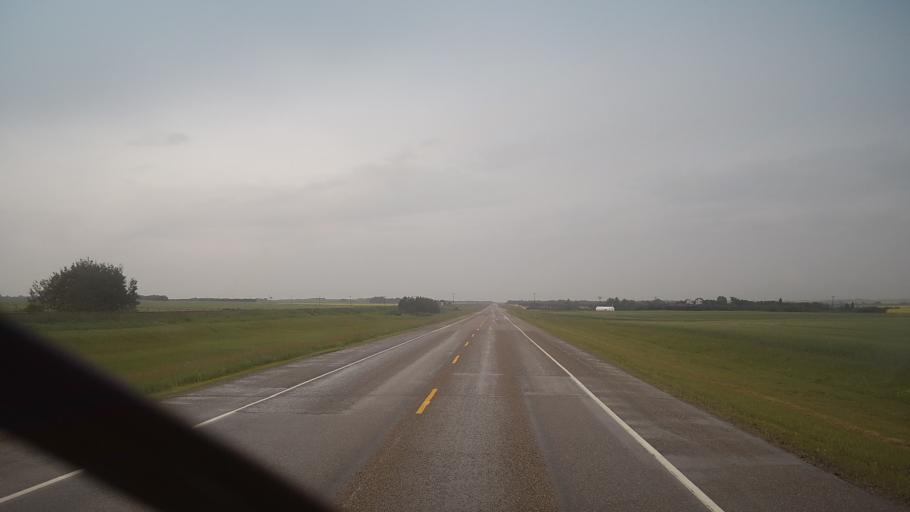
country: CA
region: Saskatchewan
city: Wilkie
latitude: 52.2283
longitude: -108.5345
